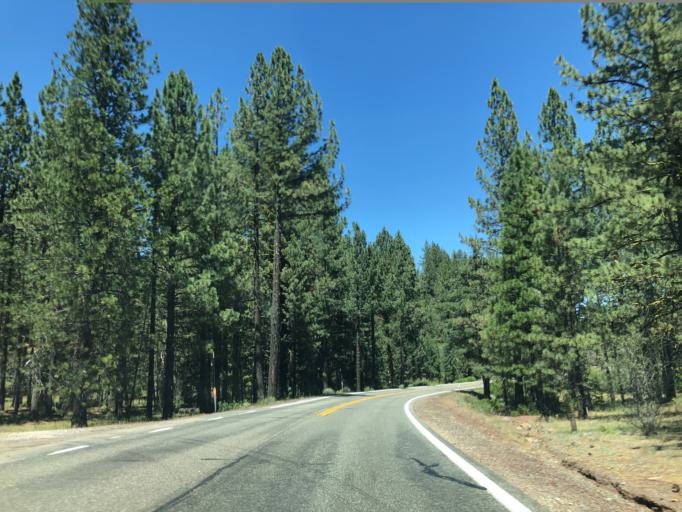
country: US
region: California
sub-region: Shasta County
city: Burney
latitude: 40.6424
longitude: -121.4717
